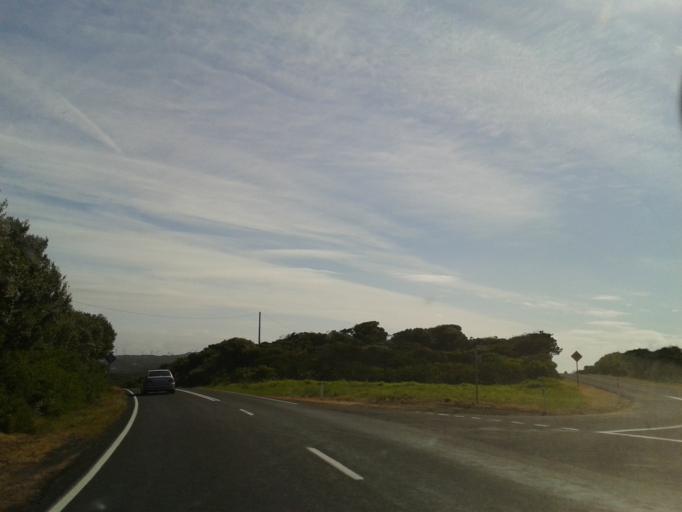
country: AU
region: Victoria
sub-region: Glenelg
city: Portland
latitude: -38.3583
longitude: 141.4348
